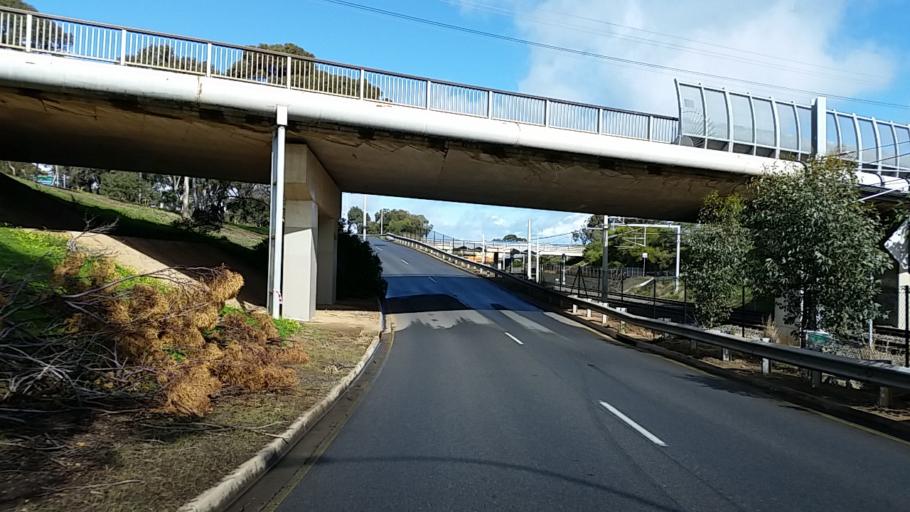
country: AU
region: South Australia
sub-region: Onkaparinga
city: Noarlunga Downs
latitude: -35.1380
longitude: 138.4935
